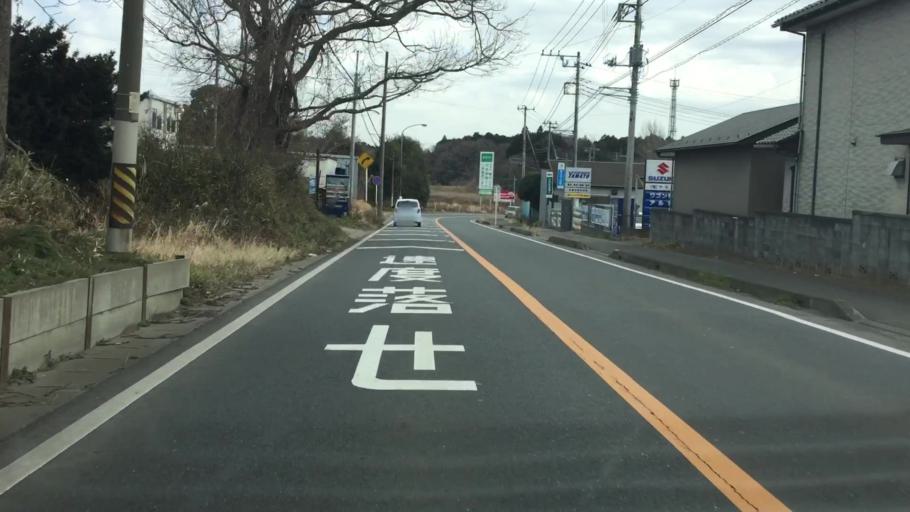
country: JP
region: Ibaraki
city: Ryugasaki
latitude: 35.8238
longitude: 140.1680
